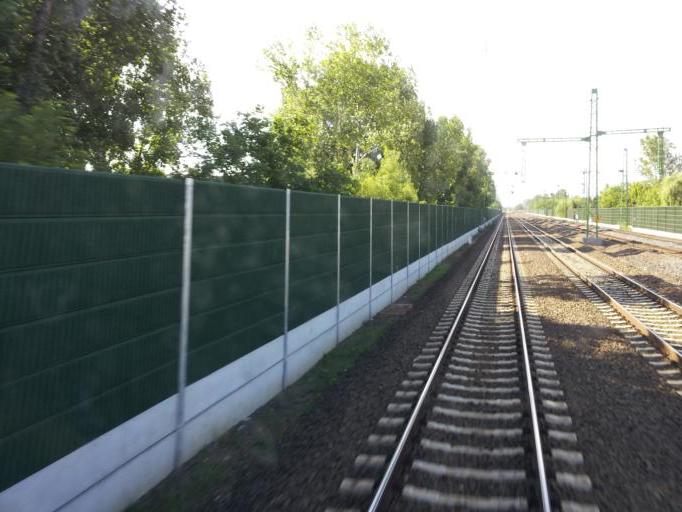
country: HU
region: Budapest
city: Budapest XXII. keruelet
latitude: 47.4486
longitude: 19.0289
